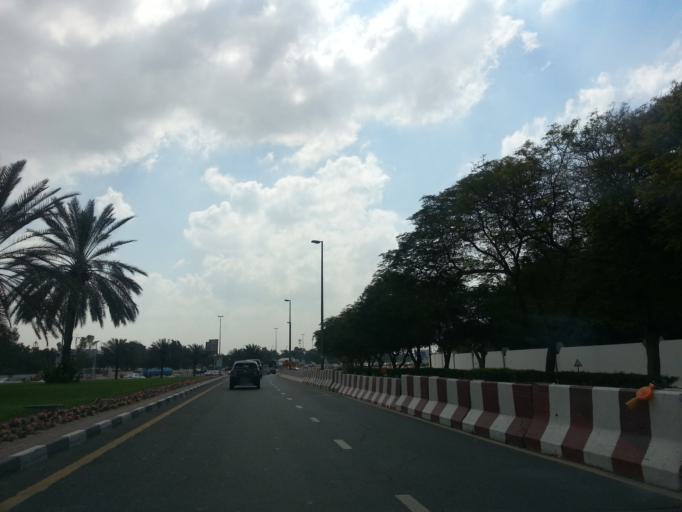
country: AE
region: Ash Shariqah
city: Sharjah
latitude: 25.2274
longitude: 55.3145
